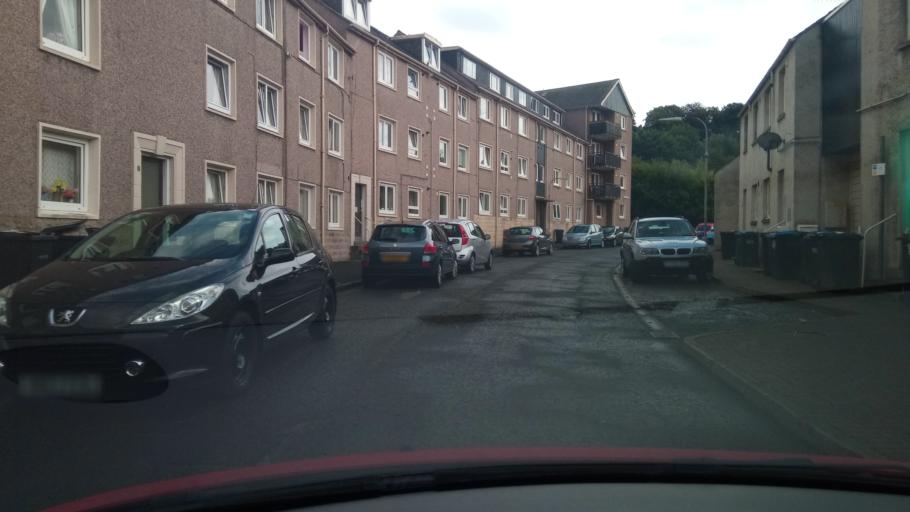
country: GB
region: Scotland
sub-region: The Scottish Borders
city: Hawick
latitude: 55.4213
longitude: -2.7863
